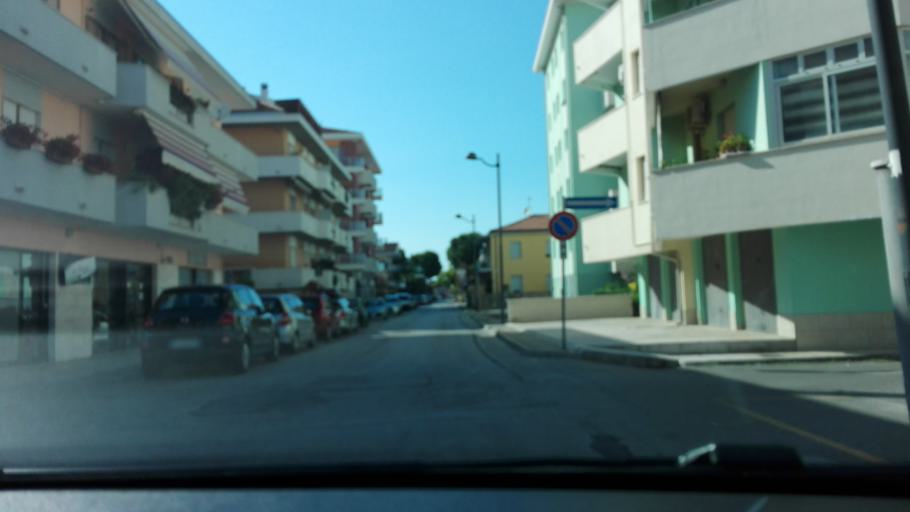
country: IT
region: Abruzzo
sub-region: Provincia di Pescara
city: Montesilvano Marina
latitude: 42.5085
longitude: 14.1656
